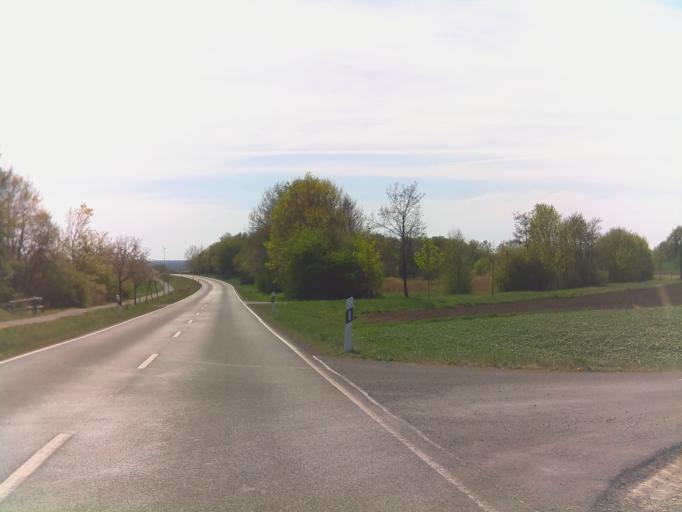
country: DE
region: Bavaria
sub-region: Regierungsbezirk Unterfranken
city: Hofheim in Unterfranken
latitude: 50.1503
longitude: 10.5453
